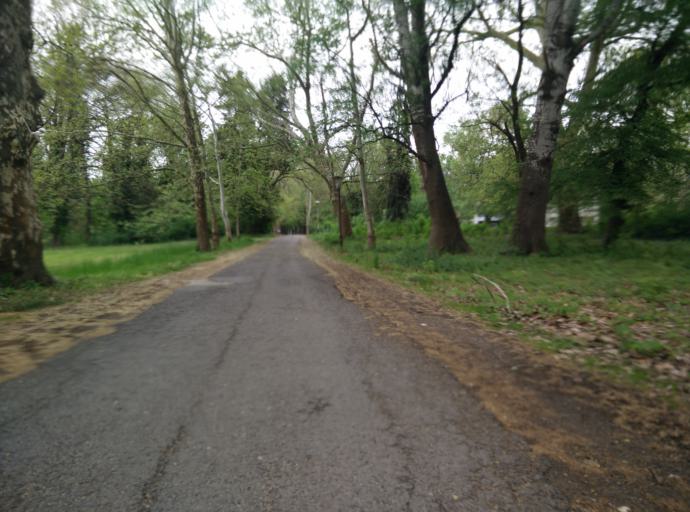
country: HU
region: Pest
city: Fot
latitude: 47.6050
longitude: 19.1898
